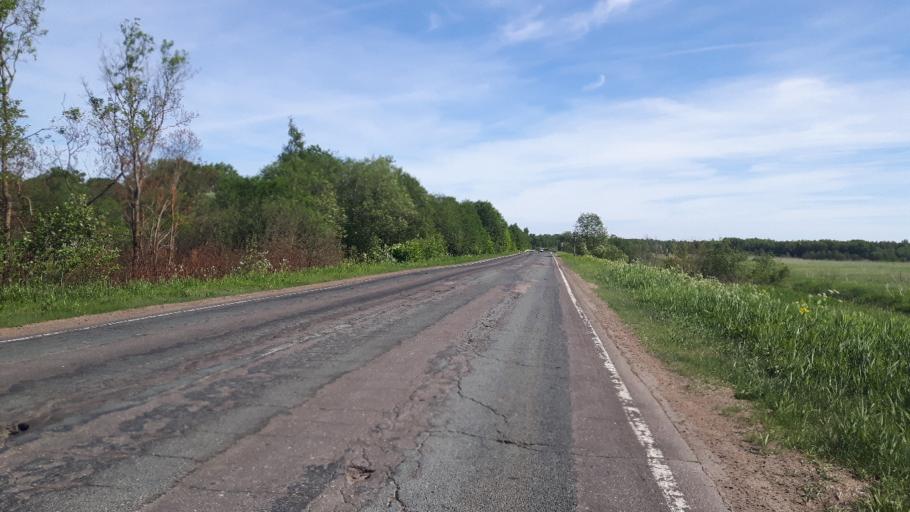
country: RU
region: Leningrad
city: Ivangorod
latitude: 59.4188
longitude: 28.3231
